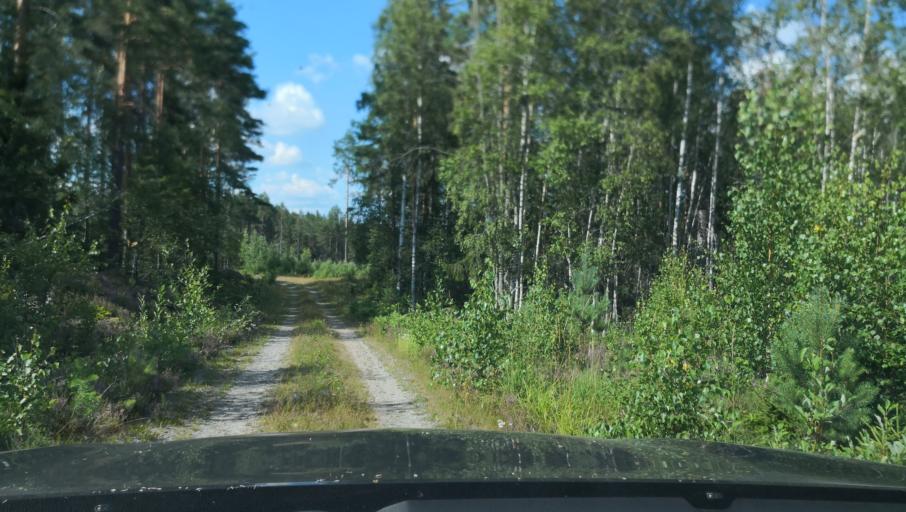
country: SE
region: Vaestmanland
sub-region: Vasteras
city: Skultuna
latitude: 59.7170
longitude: 16.3868
